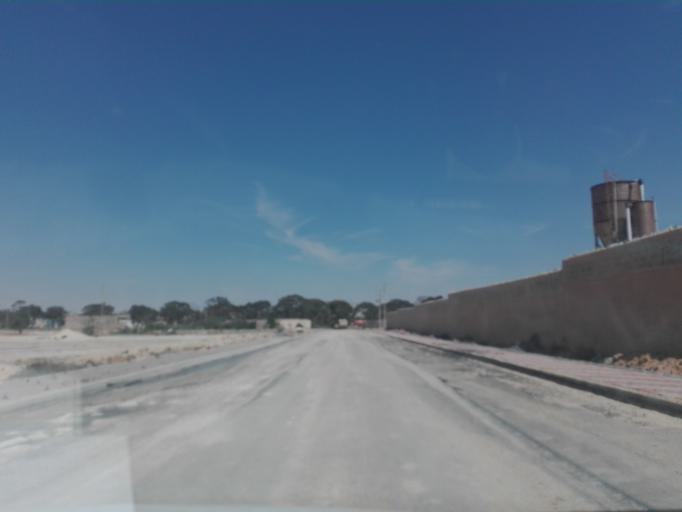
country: TN
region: Safaqis
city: Sfax
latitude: 34.7278
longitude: 10.5194
